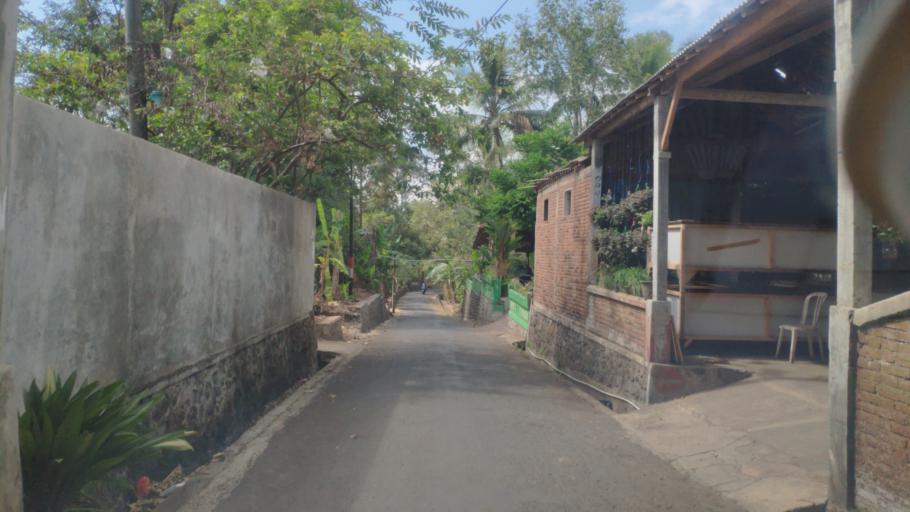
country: ID
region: Central Java
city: Wonosobo
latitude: -7.3667
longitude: 109.6344
